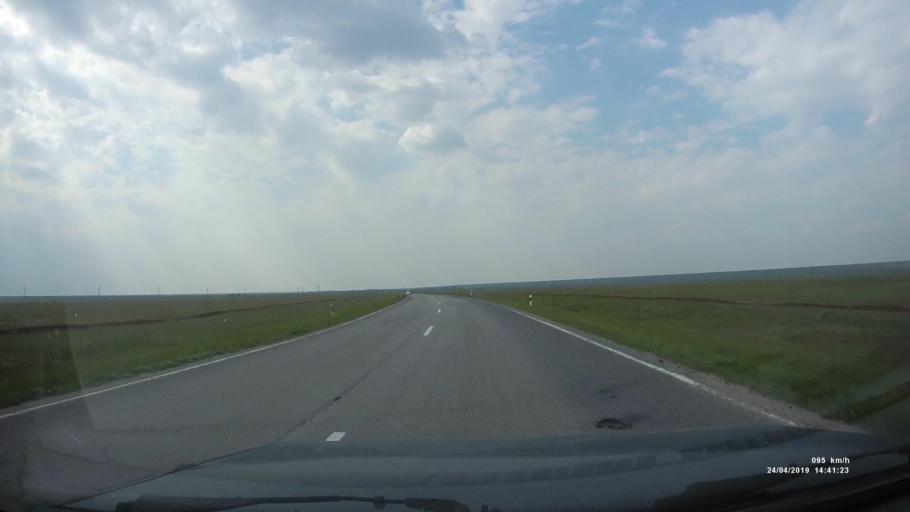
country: RU
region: Rostov
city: Remontnoye
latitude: 46.4446
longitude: 43.8807
